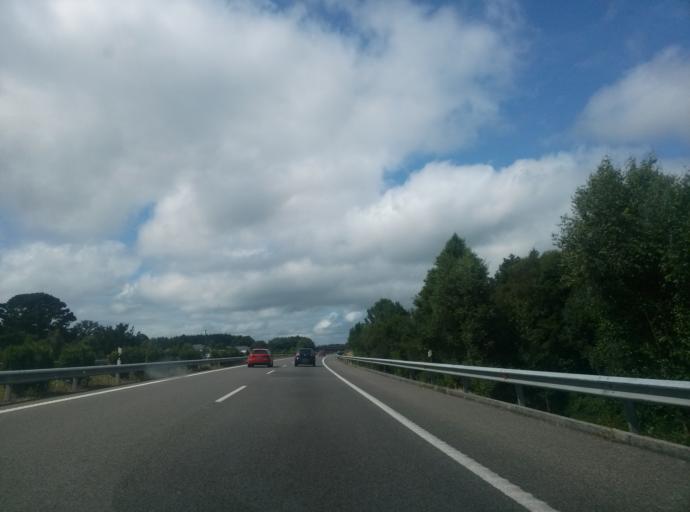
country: ES
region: Galicia
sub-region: Provincia de Lugo
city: Outeiro de Rei
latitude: 43.0766
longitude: -7.5775
